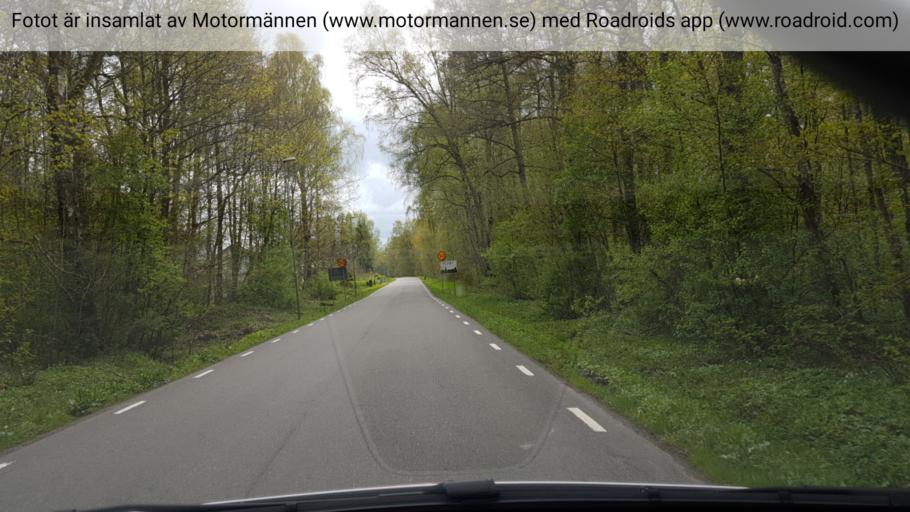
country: SE
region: Vaestra Goetaland
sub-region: Falkopings Kommun
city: Floby
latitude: 58.1500
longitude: 13.3312
